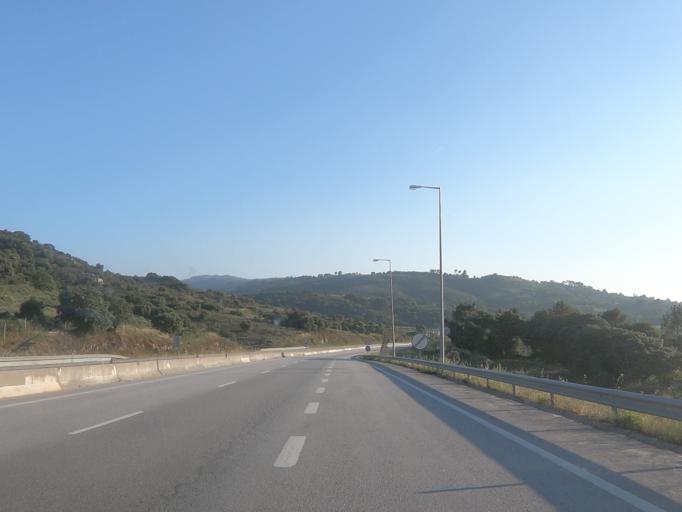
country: PT
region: Guarda
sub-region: Celorico da Beira
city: Celorico da Beira
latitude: 40.6286
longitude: -7.3589
